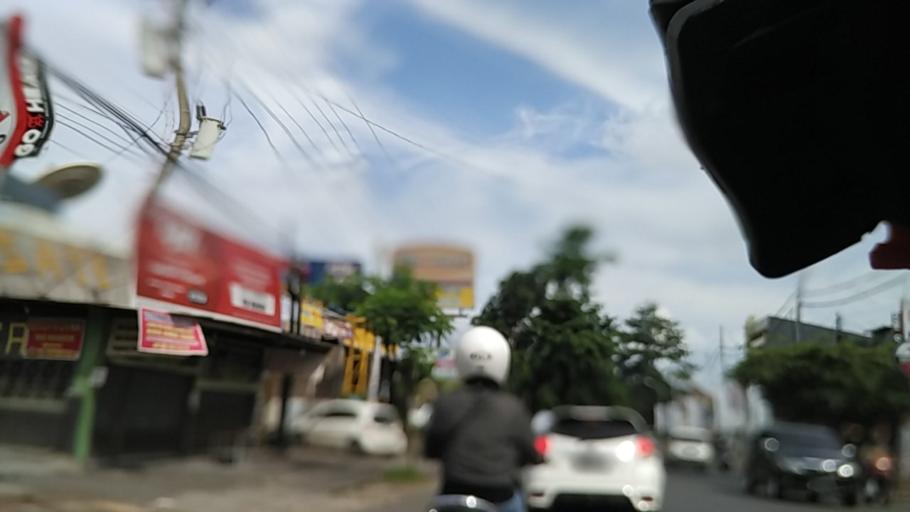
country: ID
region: Central Java
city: Semarang
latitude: -7.0506
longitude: 110.4239
